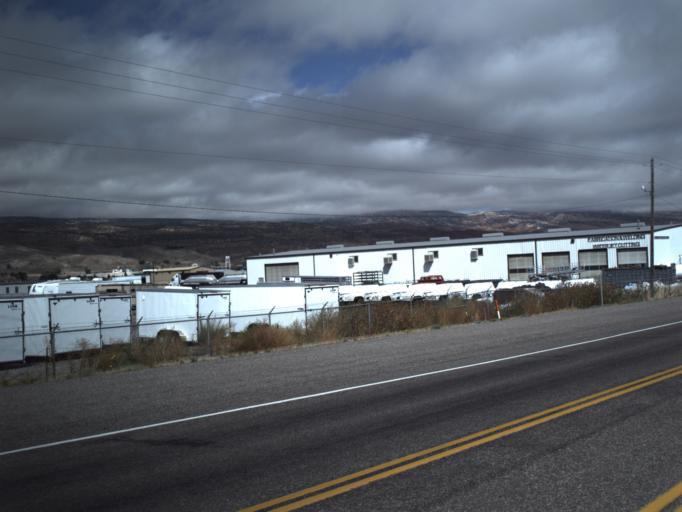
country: US
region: Utah
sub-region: Sevier County
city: Richfield
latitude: 38.7362
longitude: -112.0943
